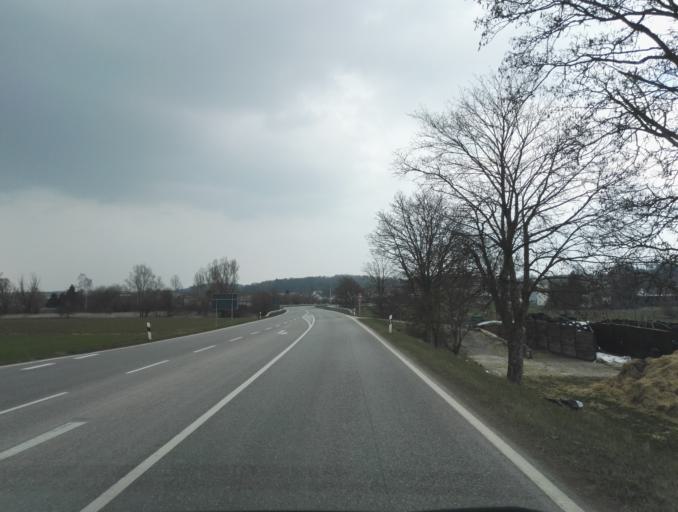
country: DE
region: Bavaria
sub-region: Lower Bavaria
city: Rottenburg an der Laaber
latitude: 48.7114
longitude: 12.0114
